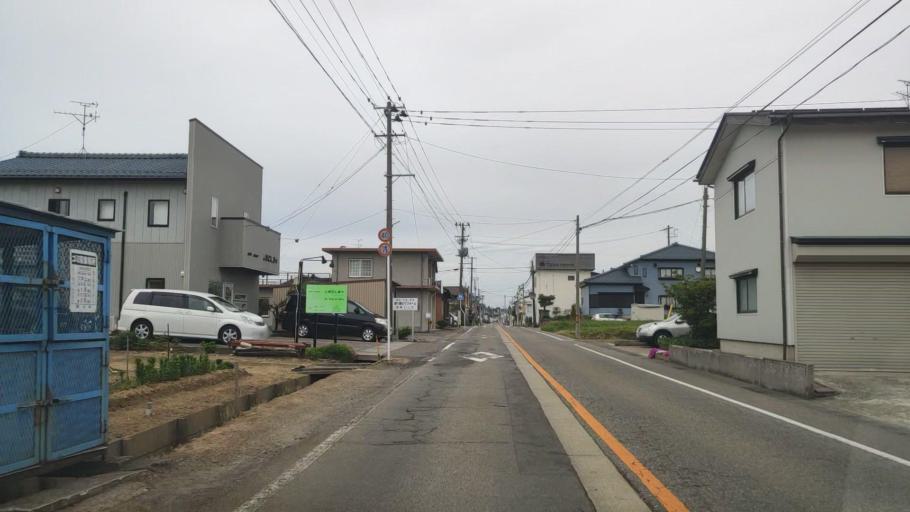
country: JP
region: Niigata
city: Kamo
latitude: 37.7169
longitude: 139.0737
